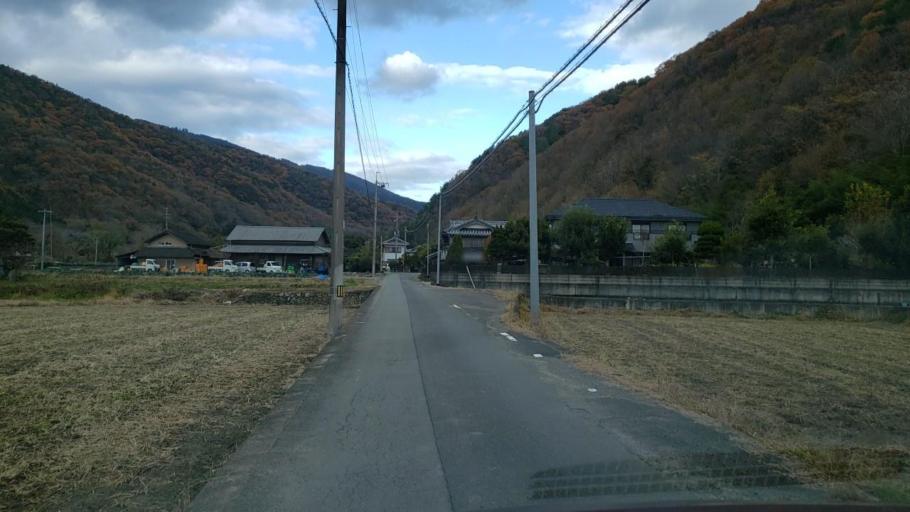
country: JP
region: Tokushima
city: Wakimachi
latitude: 34.1043
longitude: 134.2249
